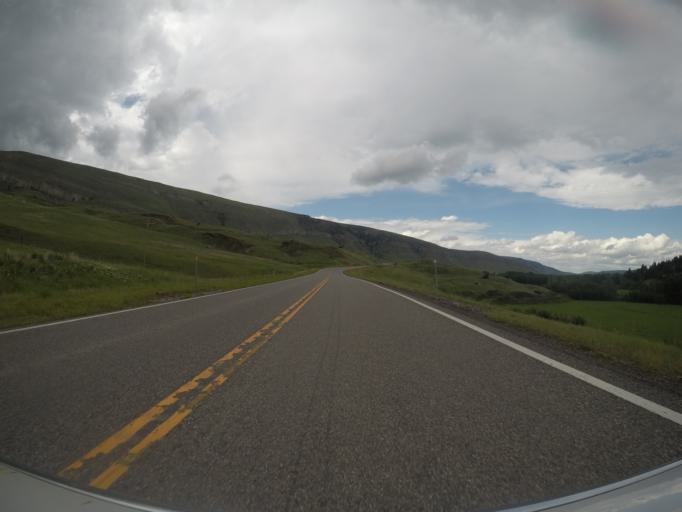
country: US
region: Montana
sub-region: Sweet Grass County
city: Big Timber
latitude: 45.5631
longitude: -110.2019
